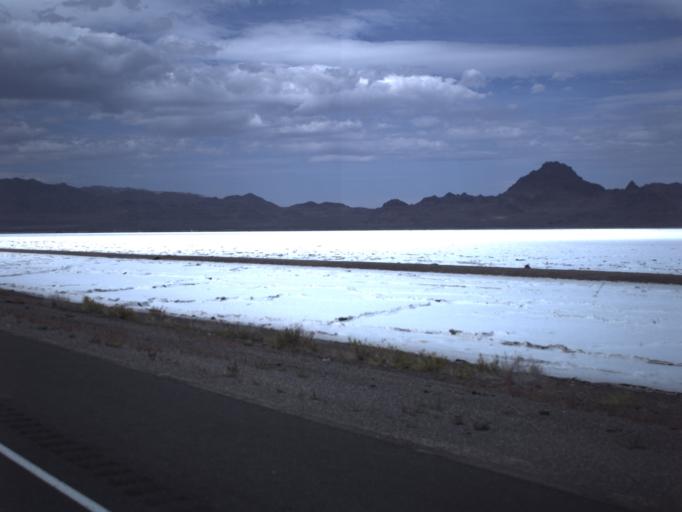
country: US
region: Utah
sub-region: Tooele County
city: Wendover
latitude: 40.7408
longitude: -113.9212
